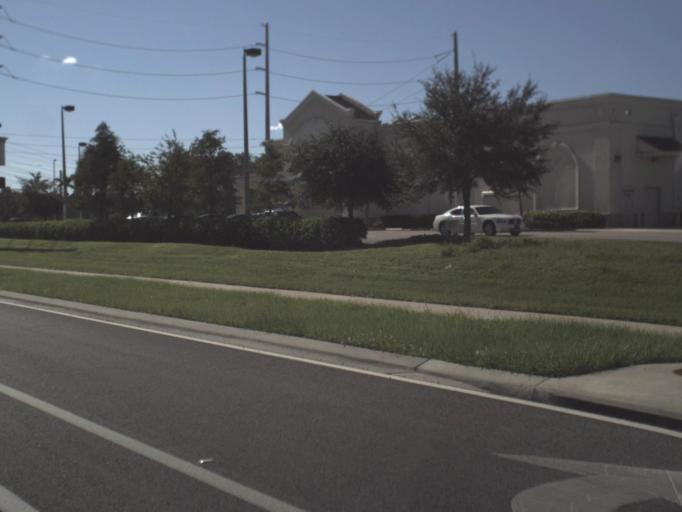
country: US
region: Florida
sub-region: Lee County
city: Gateway
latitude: 26.6195
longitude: -81.7691
